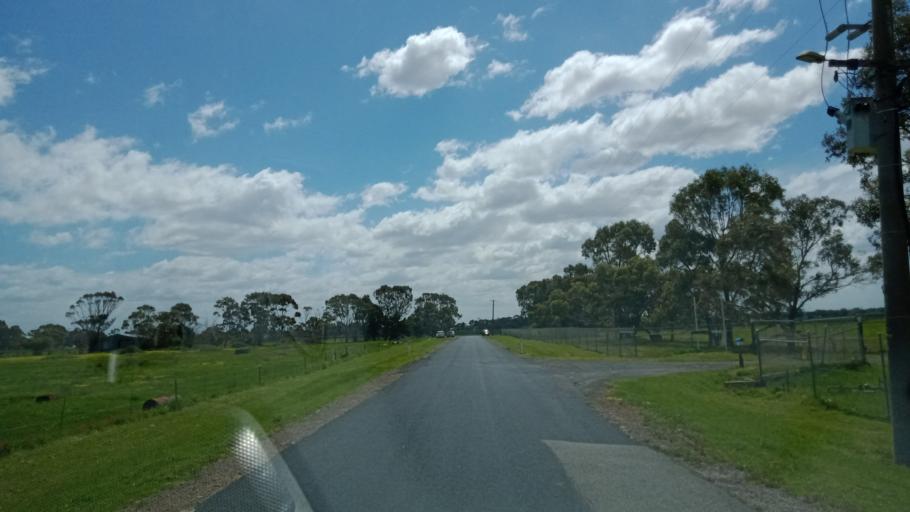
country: AU
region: Victoria
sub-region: Kingston
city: Chelsea Heights
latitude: -38.0387
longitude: 145.1441
